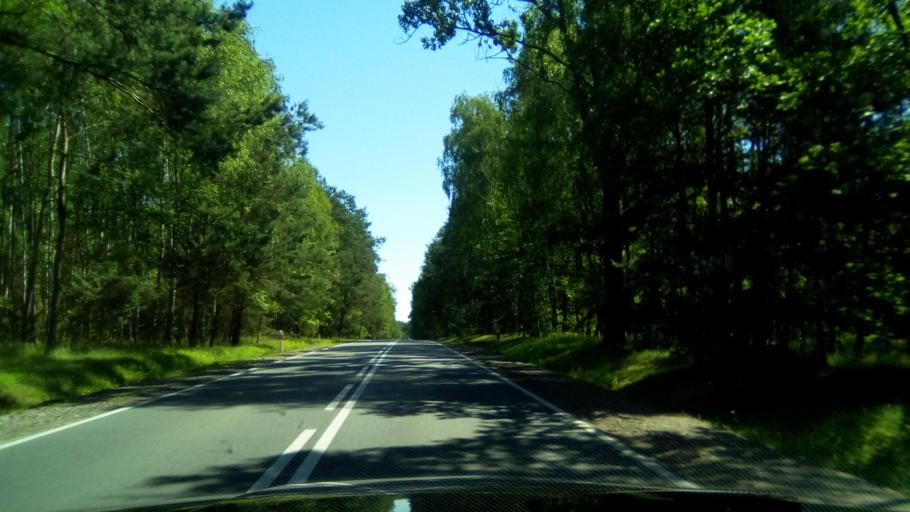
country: PL
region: Masovian Voivodeship
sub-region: Powiat przysuski
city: Odrzywol
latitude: 51.5261
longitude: 20.5923
